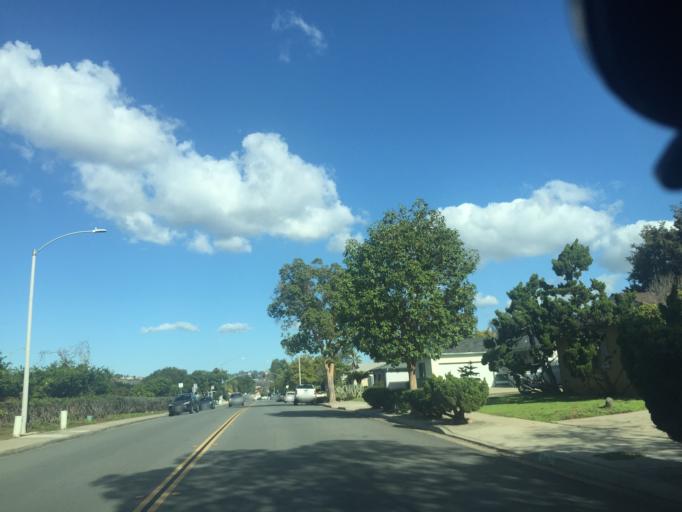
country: US
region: California
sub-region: San Diego County
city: La Mesa
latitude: 32.7916
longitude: -117.0938
